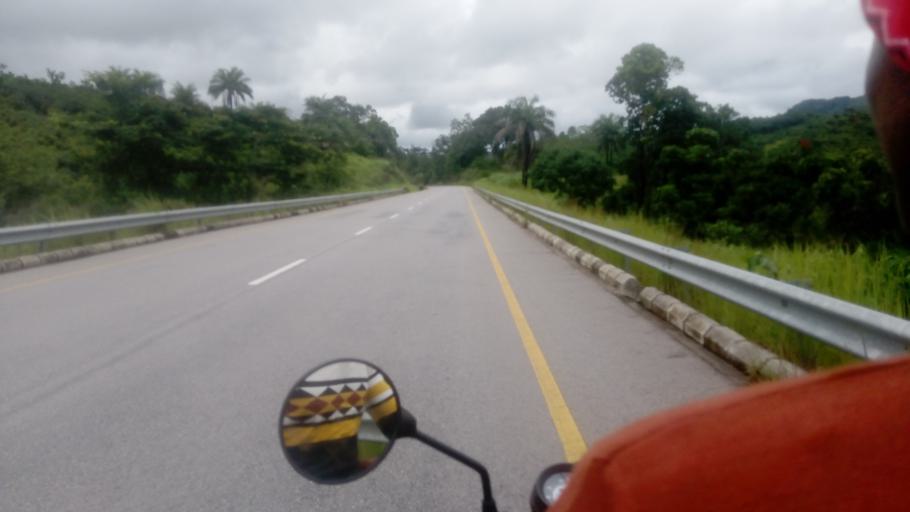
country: SL
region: Northern Province
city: Masaka
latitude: 8.6437
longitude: -11.7428
